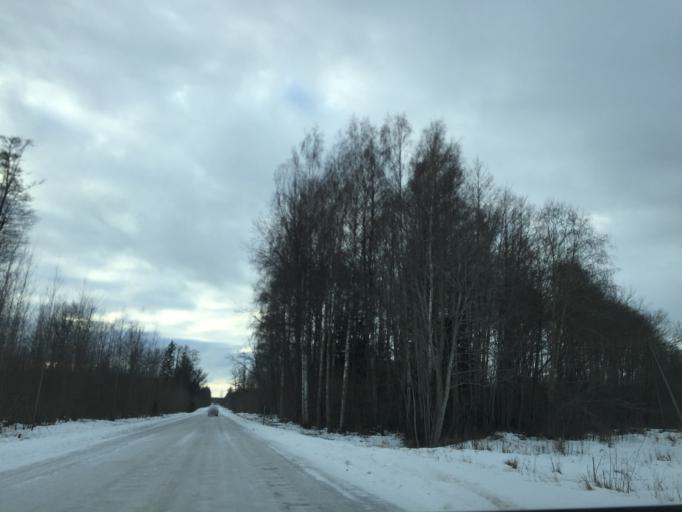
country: LV
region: Lielvarde
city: Lielvarde
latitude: 56.5991
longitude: 24.7417
